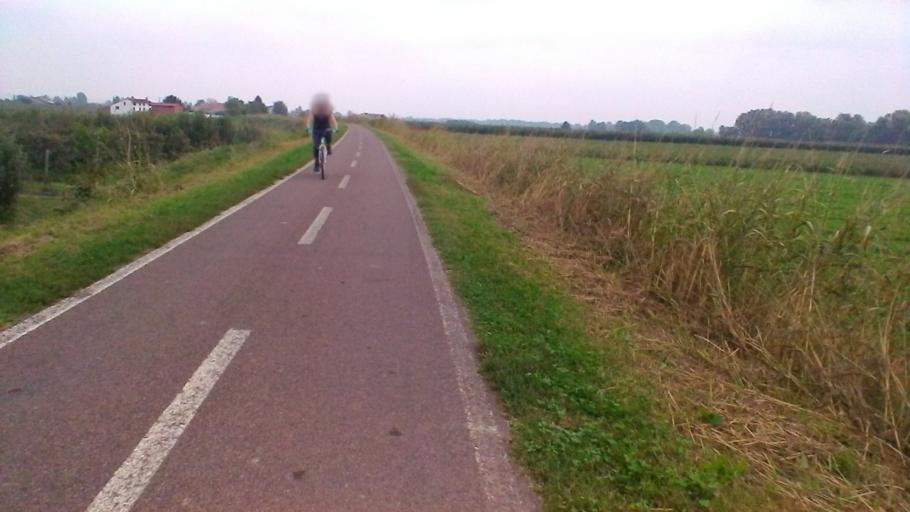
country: IT
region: Veneto
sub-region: Provincia di Verona
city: San Martino Buon Albergo
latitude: 45.3858
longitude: 11.0926
